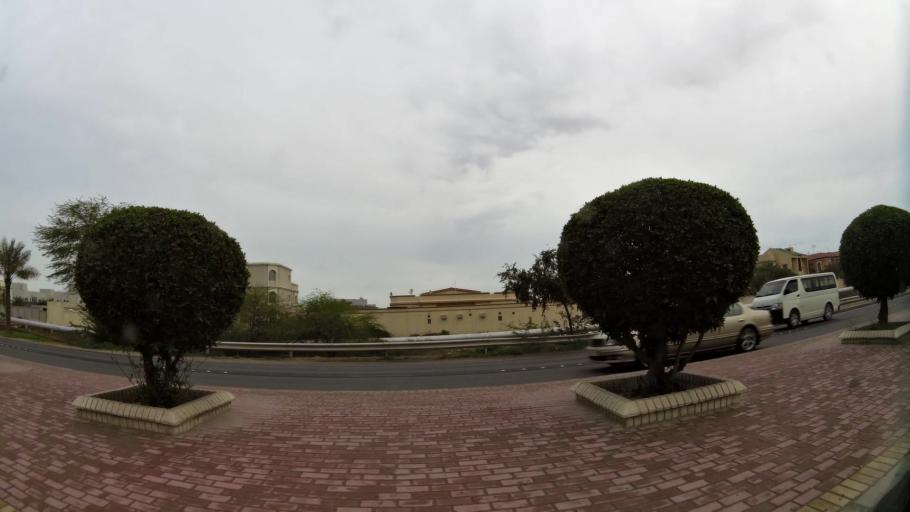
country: BH
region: Central Governorate
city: Madinat Hamad
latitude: 26.1378
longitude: 50.5209
